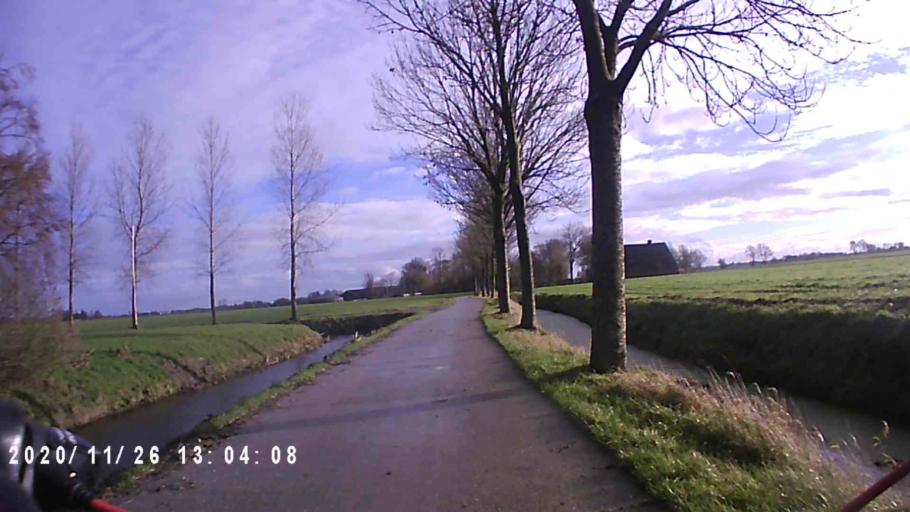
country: NL
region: Groningen
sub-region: Gemeente Appingedam
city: Appingedam
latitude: 53.3536
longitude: 6.8314
